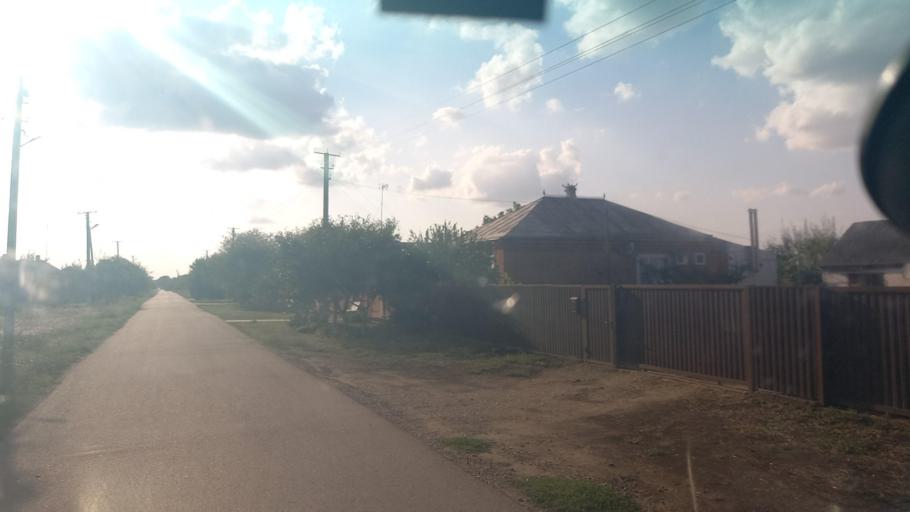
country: RU
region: Adygeya
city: Khatukay
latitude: 45.2991
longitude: 39.5688
